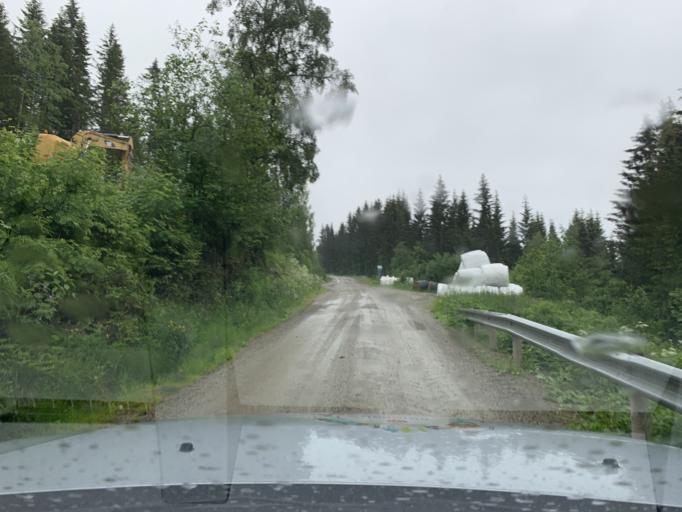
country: NO
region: Oppland
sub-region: Oyer
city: Tretten
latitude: 61.3858
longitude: 10.2836
